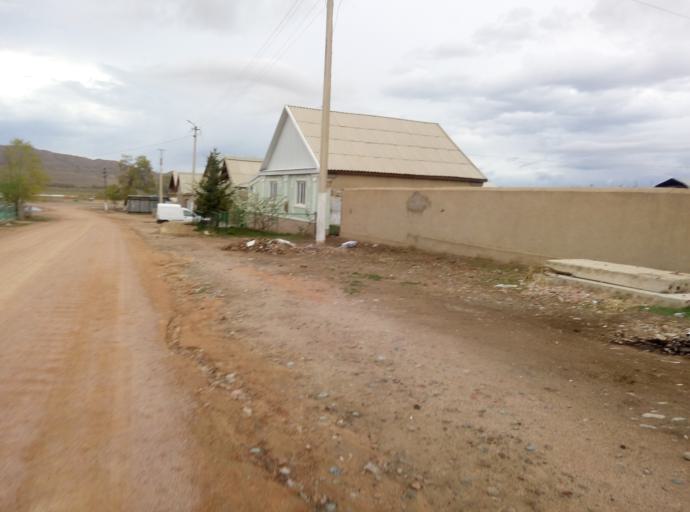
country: KG
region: Ysyk-Koel
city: Bokombayevskoye
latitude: 42.1145
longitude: 76.9798
